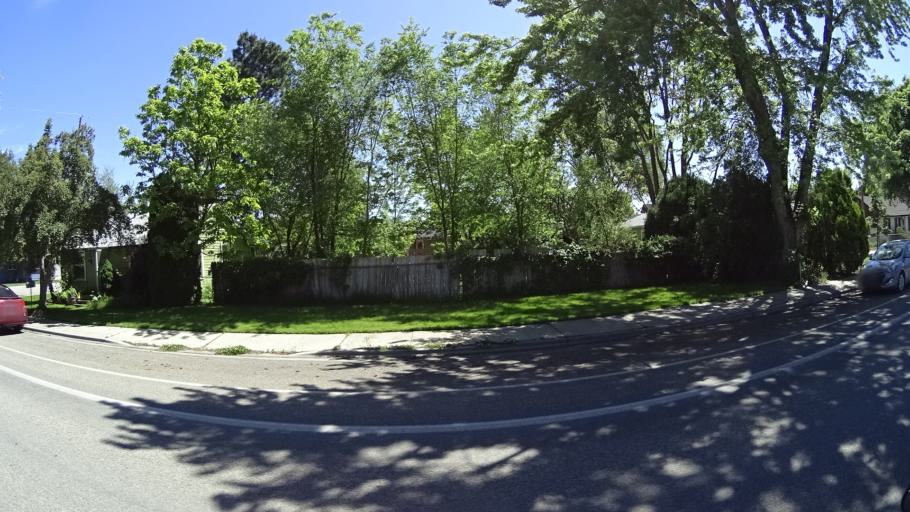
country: US
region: Idaho
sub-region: Ada County
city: Boise
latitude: 43.5802
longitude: -116.1836
